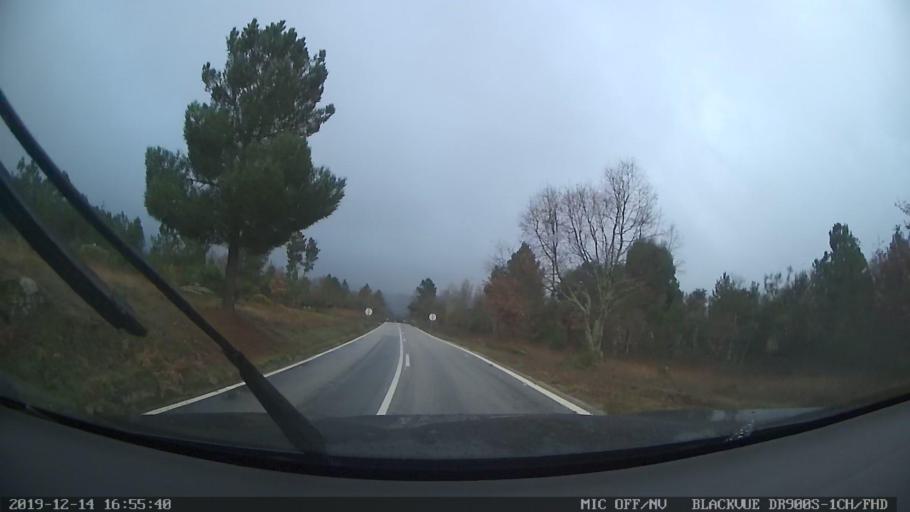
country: PT
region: Vila Real
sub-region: Murca
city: Murca
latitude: 41.4393
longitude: -7.5329
